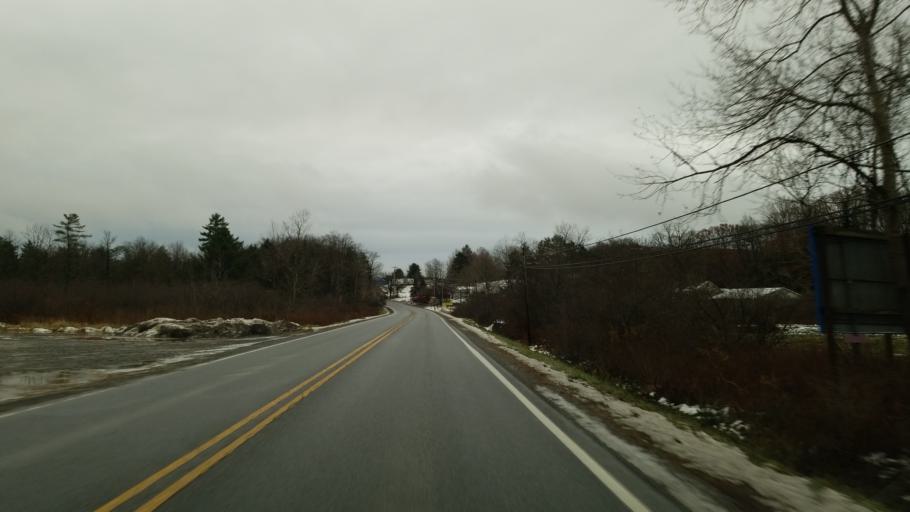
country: US
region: Pennsylvania
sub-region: Clearfield County
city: DuBois
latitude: 41.1109
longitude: -78.7238
